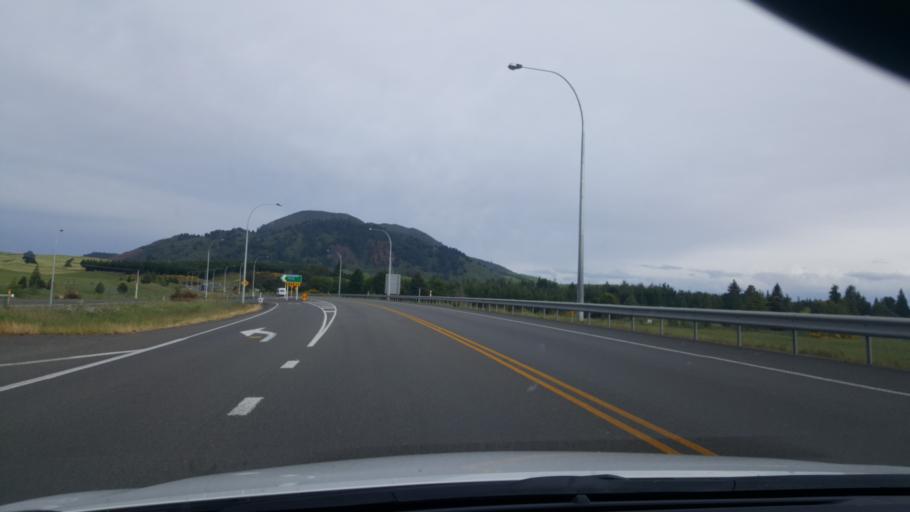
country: NZ
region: Waikato
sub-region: Taupo District
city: Taupo
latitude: -38.6688
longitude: 176.1045
